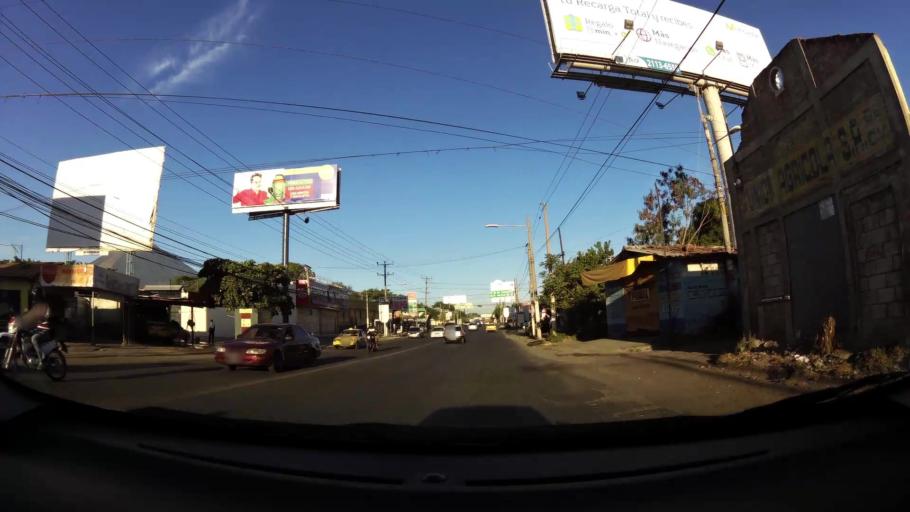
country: SV
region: San Miguel
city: San Miguel
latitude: 13.4668
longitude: -88.1746
